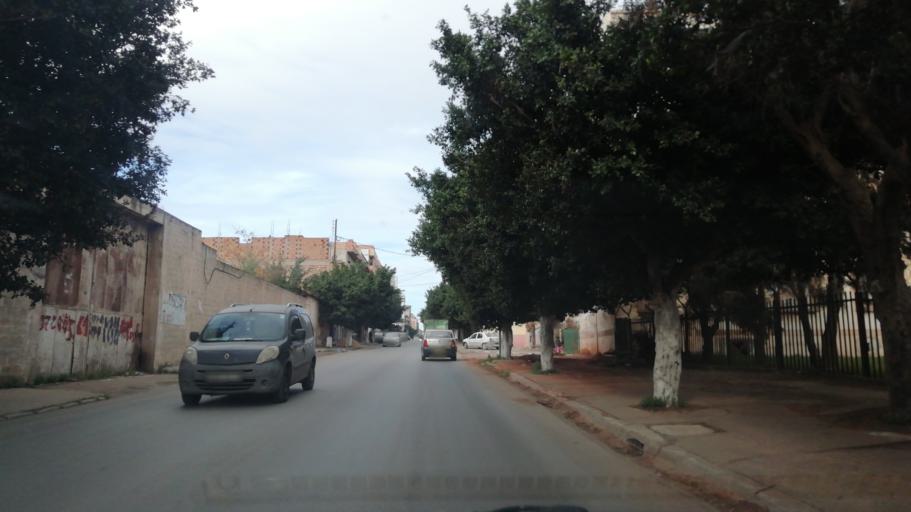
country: DZ
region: Oran
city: Oran
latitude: 35.6858
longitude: -0.6174
